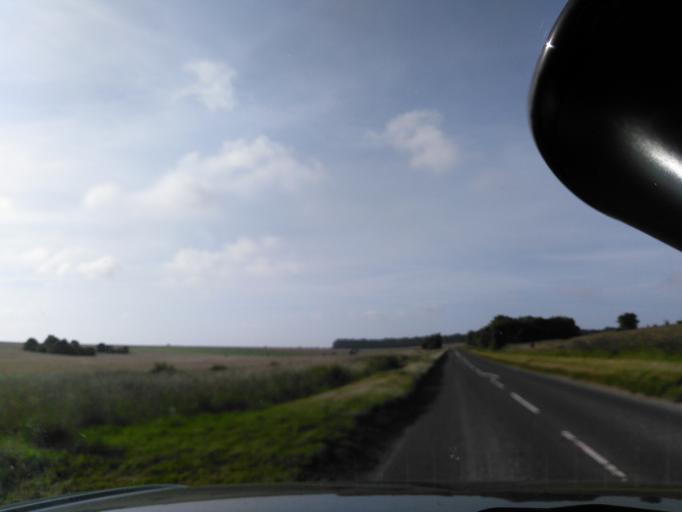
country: GB
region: England
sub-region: Wiltshire
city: Market Lavington
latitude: 51.2381
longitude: -1.9732
